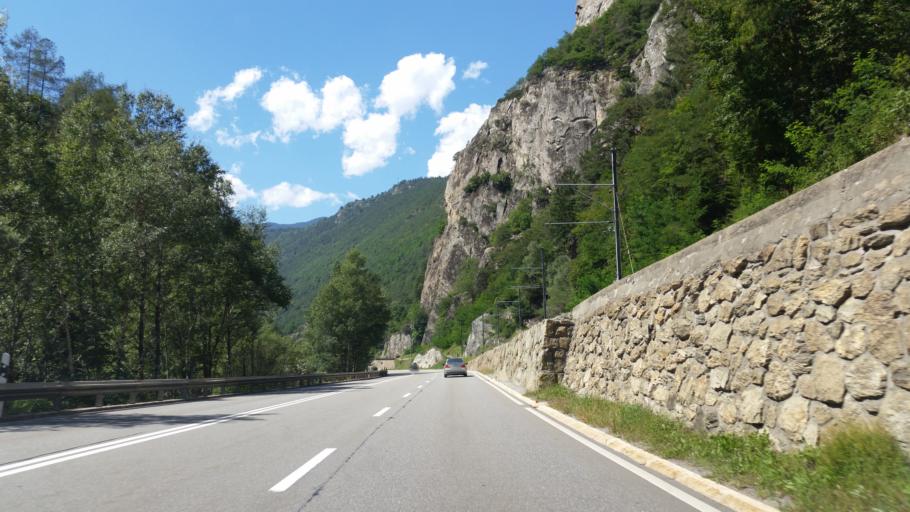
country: CH
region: Valais
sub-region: Martigny District
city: Martigny-Ville
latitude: 46.0814
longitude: 7.1075
